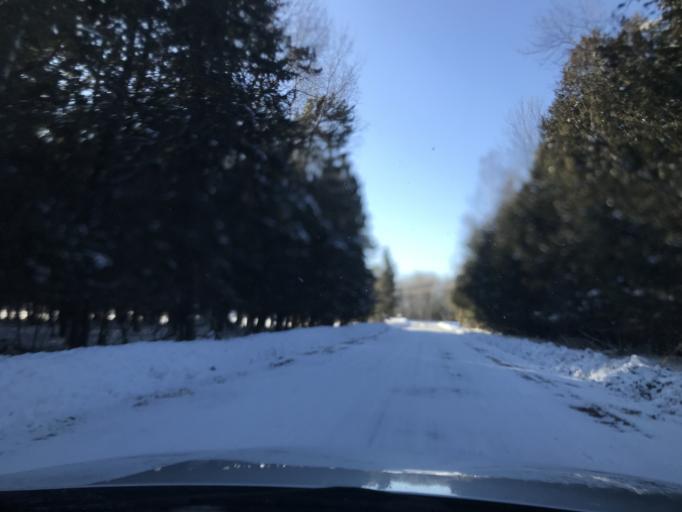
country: US
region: Wisconsin
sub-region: Oconto County
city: Oconto
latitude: 44.9519
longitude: -87.9770
